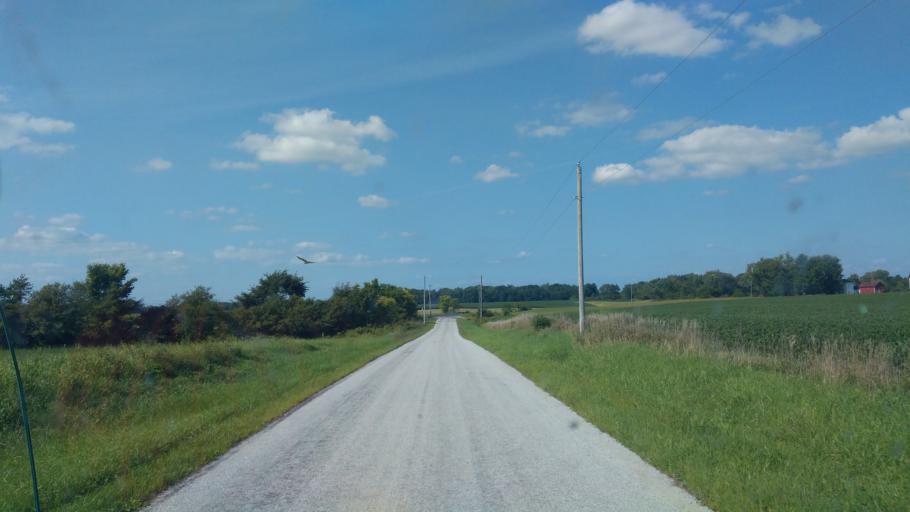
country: US
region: Ohio
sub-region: Hardin County
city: Forest
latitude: 40.6993
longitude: -83.4602
